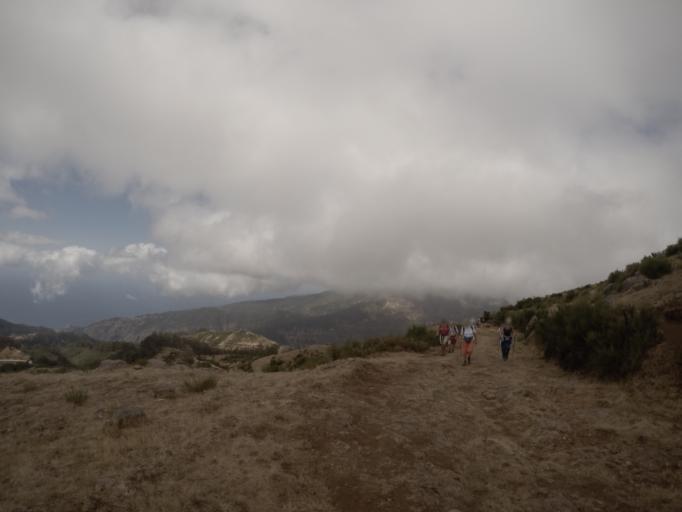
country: PT
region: Madeira
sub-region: Camara de Lobos
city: Curral das Freiras
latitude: 32.7143
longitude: -17.0058
